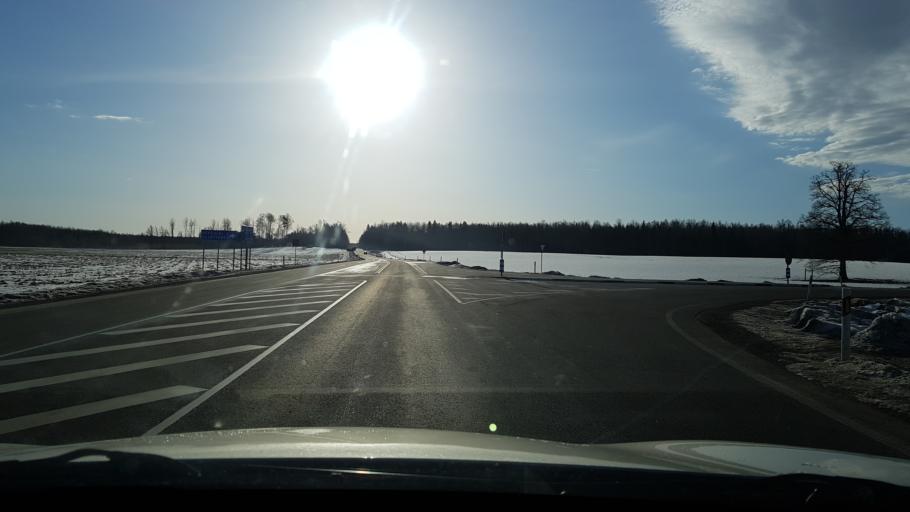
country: EE
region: Viljandimaa
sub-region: Vohma linn
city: Vohma
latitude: 58.5666
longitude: 25.5753
